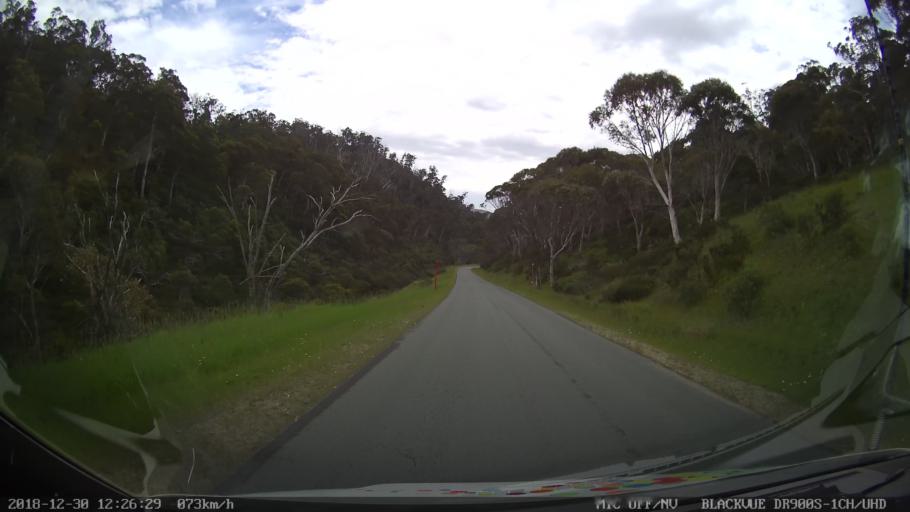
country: AU
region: New South Wales
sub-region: Snowy River
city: Jindabyne
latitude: -36.3387
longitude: 148.4894
